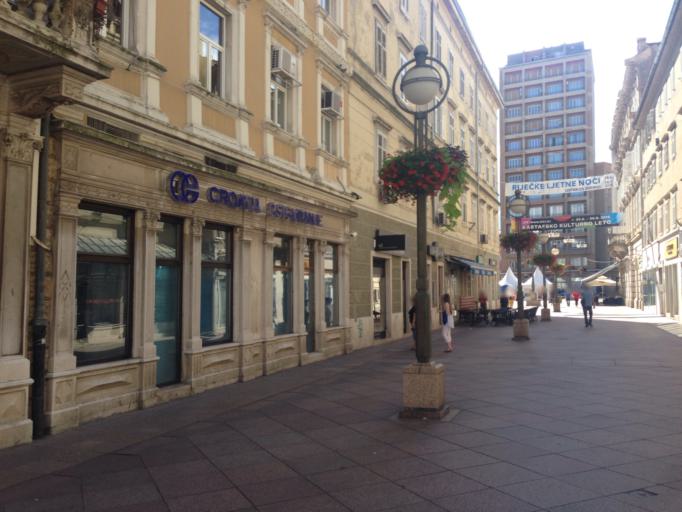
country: HR
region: Primorsko-Goranska
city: Drenova
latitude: 45.3276
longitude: 14.4401
